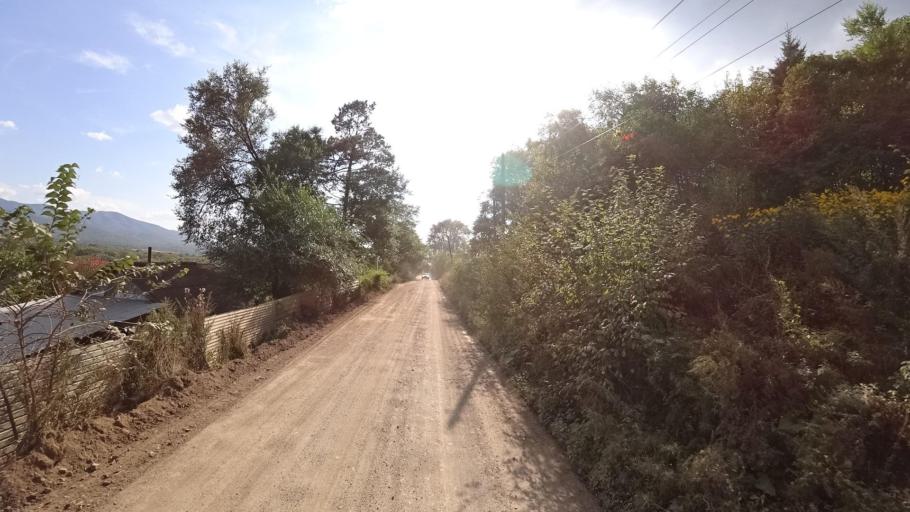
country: RU
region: Jewish Autonomous Oblast
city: Birakan
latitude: 48.9994
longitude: 131.7278
